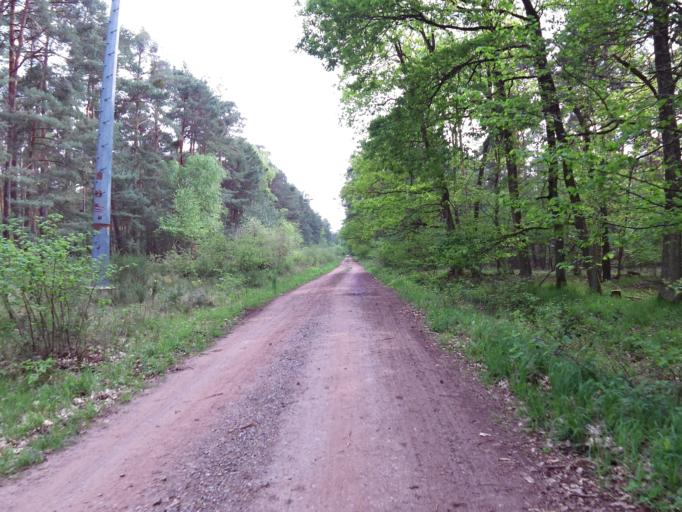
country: DE
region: Rheinland-Pfalz
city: Lachen-Speyerdorf
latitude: 49.3438
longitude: 8.2274
